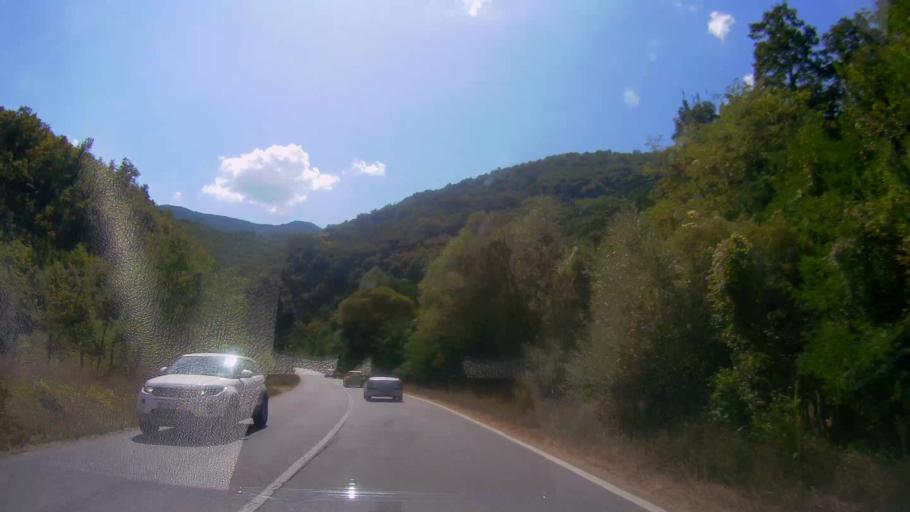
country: BG
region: Stara Zagora
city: Gurkovo
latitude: 42.7120
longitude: 25.7170
